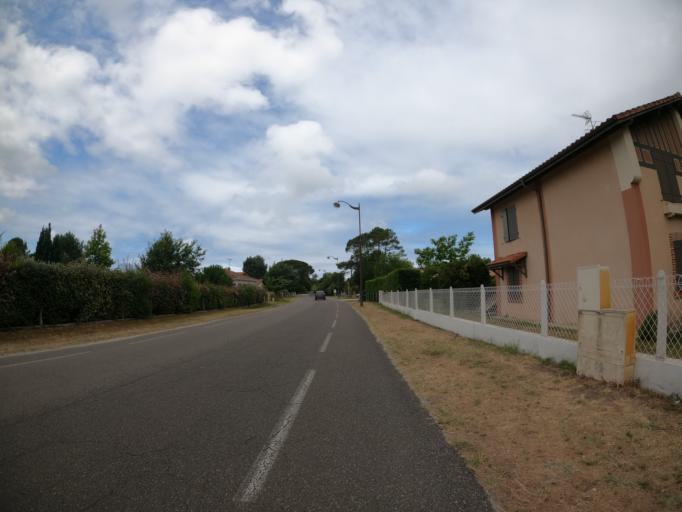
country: FR
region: Aquitaine
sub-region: Departement des Landes
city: Leon
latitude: 43.8828
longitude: -1.3090
